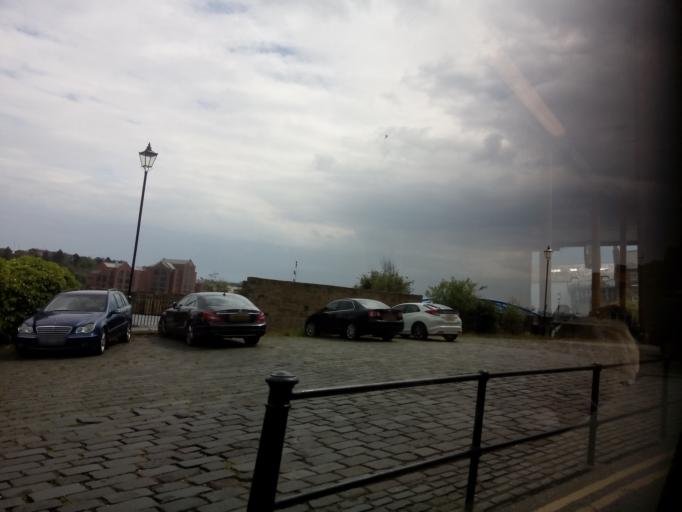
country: GB
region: England
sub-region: Borough of North Tyneside
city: North Shields
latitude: 55.0044
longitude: -1.4441
